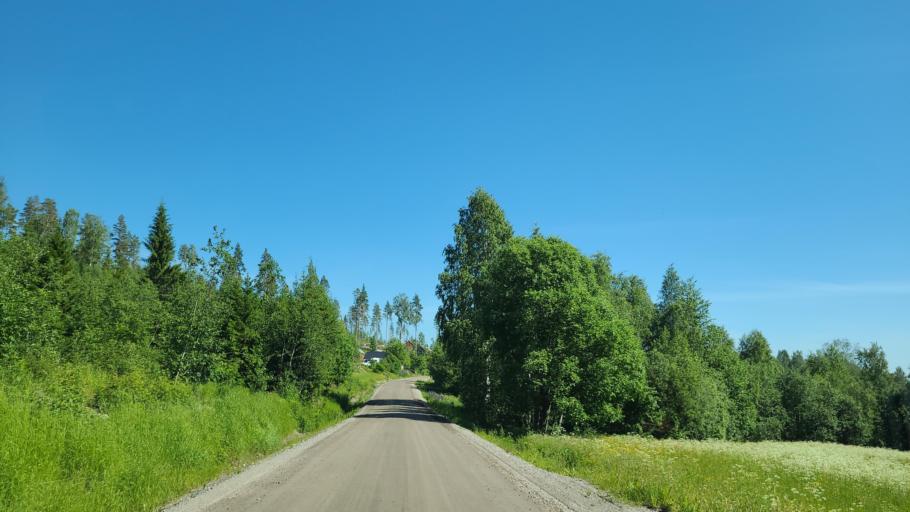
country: SE
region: Vaesterbotten
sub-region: Bjurholms Kommun
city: Bjurholm
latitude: 63.6756
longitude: 19.0198
